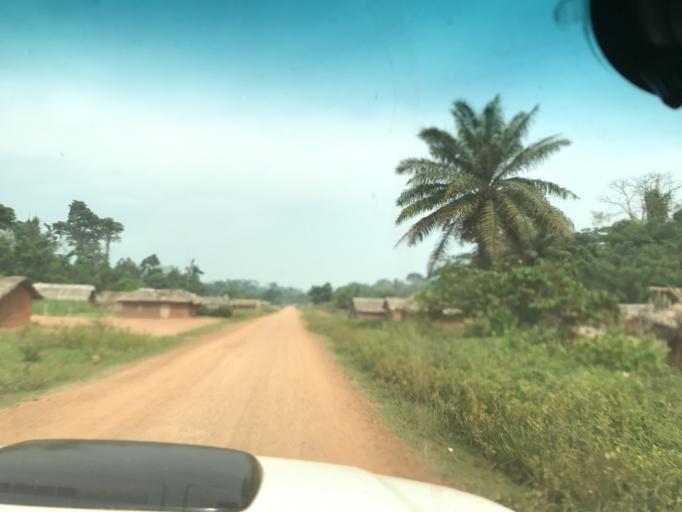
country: CD
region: Eastern Province
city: Buta
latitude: 2.8573
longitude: 24.5062
